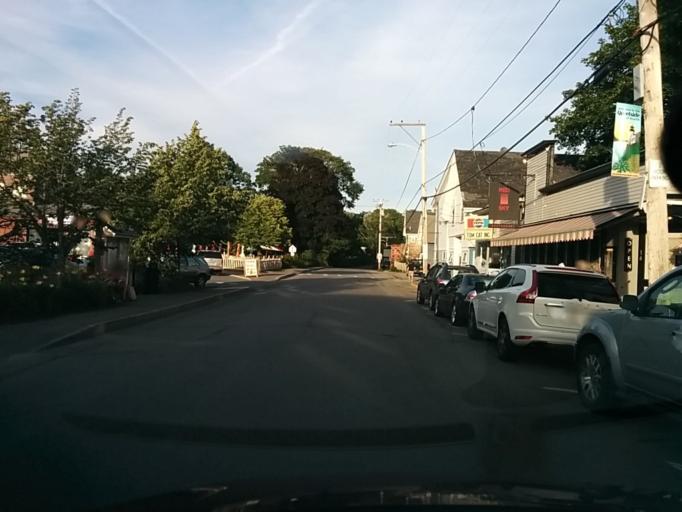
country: US
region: Maine
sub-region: Hancock County
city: Tremont
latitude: 44.2798
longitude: -68.3254
